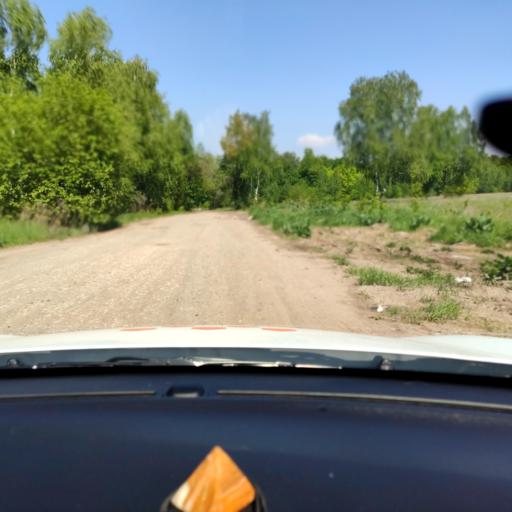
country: RU
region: Tatarstan
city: Stolbishchi
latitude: 55.7092
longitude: 49.1897
